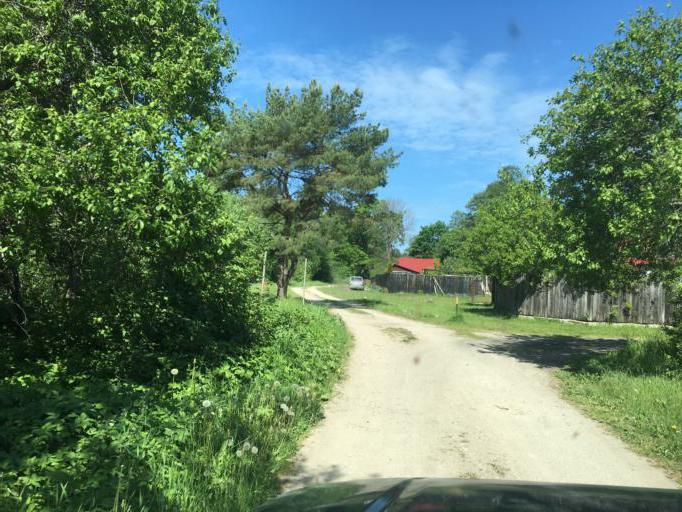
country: LV
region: Ventspils
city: Ventspils
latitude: 57.4568
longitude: 21.6513
